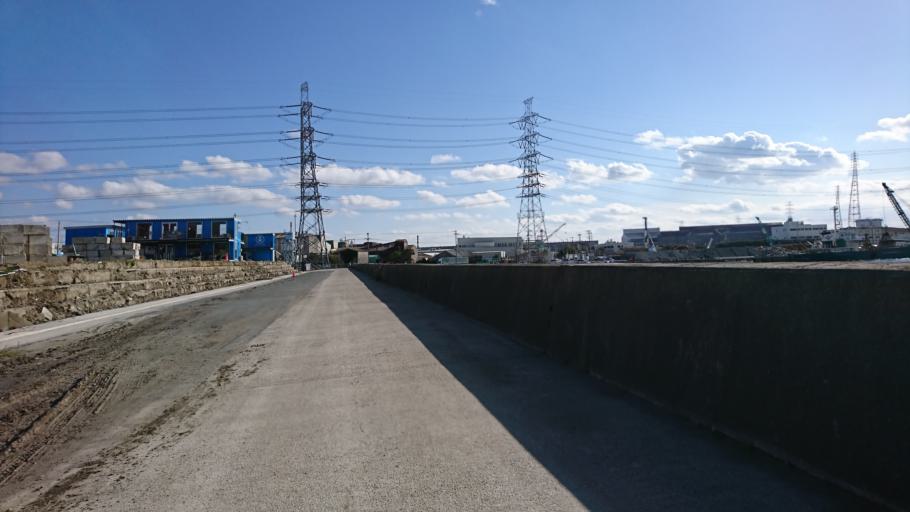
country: JP
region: Hyogo
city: Shirahamacho-usazakiminami
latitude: 34.7611
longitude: 134.7647
